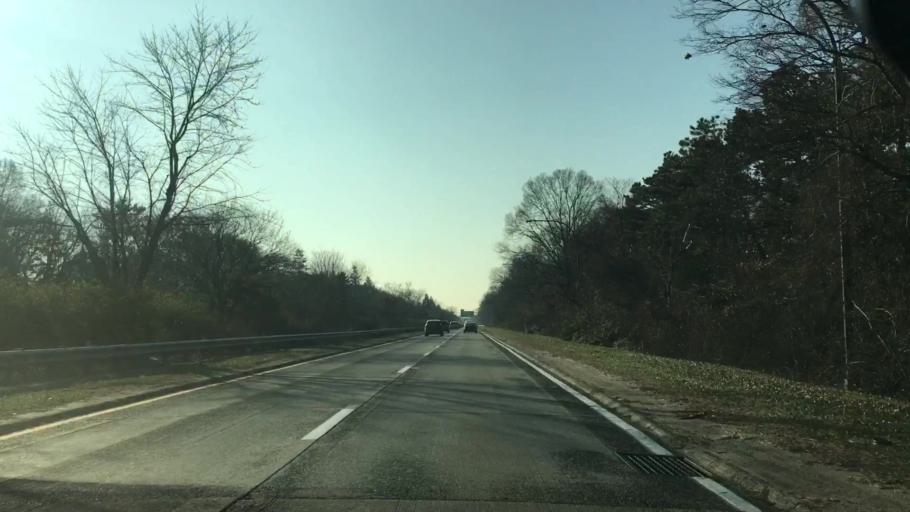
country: US
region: New York
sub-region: Suffolk County
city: Bay Wood
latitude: 40.7606
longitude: -73.2801
